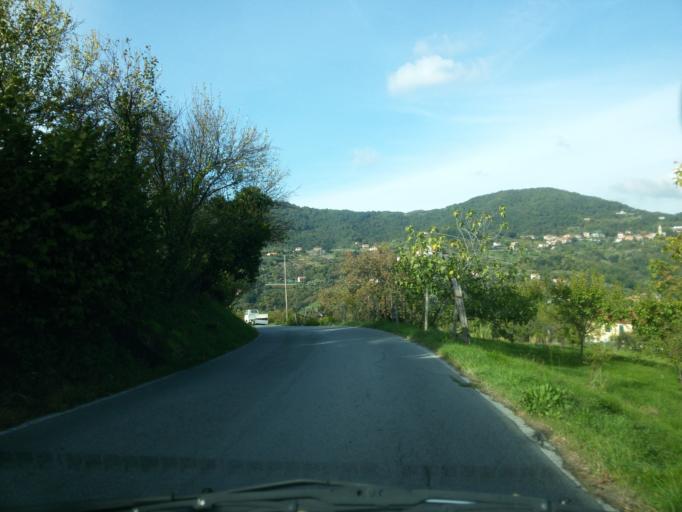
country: IT
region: Liguria
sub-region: Provincia di Genova
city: Piccarello
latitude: 44.4784
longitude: 8.9640
